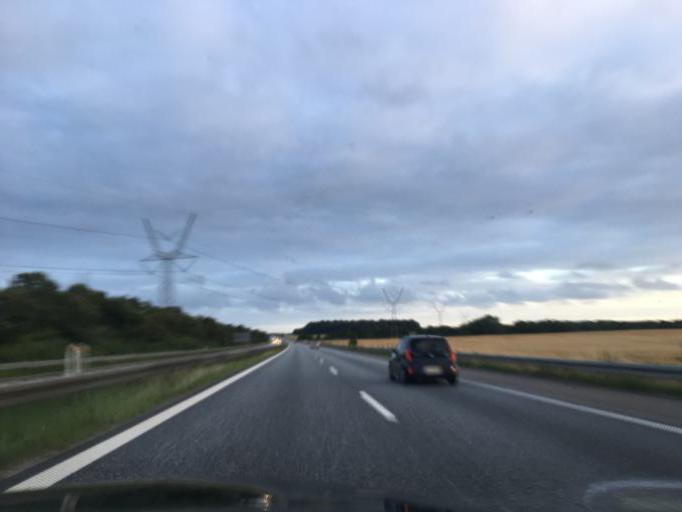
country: DK
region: South Denmark
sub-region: Kolding Kommune
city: Christiansfeld
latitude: 55.3491
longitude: 9.4453
